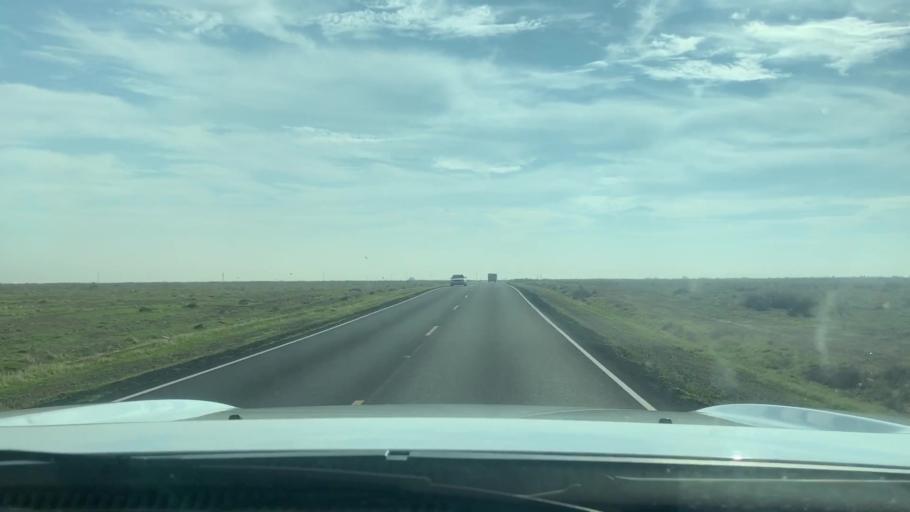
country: US
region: California
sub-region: Kern County
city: Lost Hills
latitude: 35.5708
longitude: -119.8134
